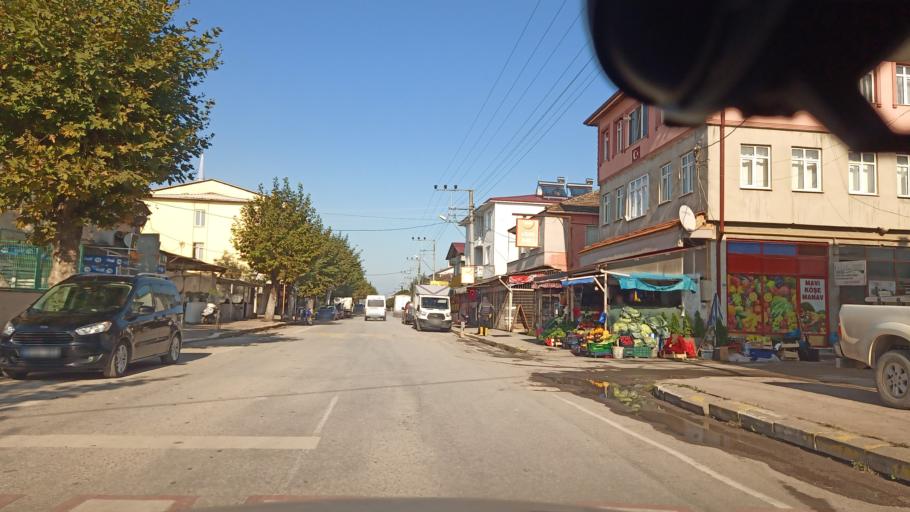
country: TR
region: Sakarya
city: Sogutlu
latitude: 40.8805
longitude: 30.4628
